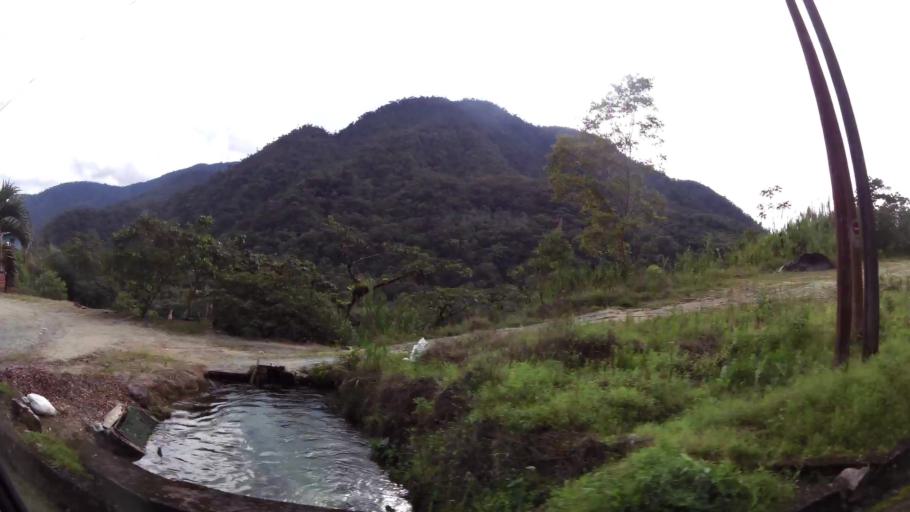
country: EC
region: Pastaza
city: Puyo
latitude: -1.4213
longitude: -78.1749
